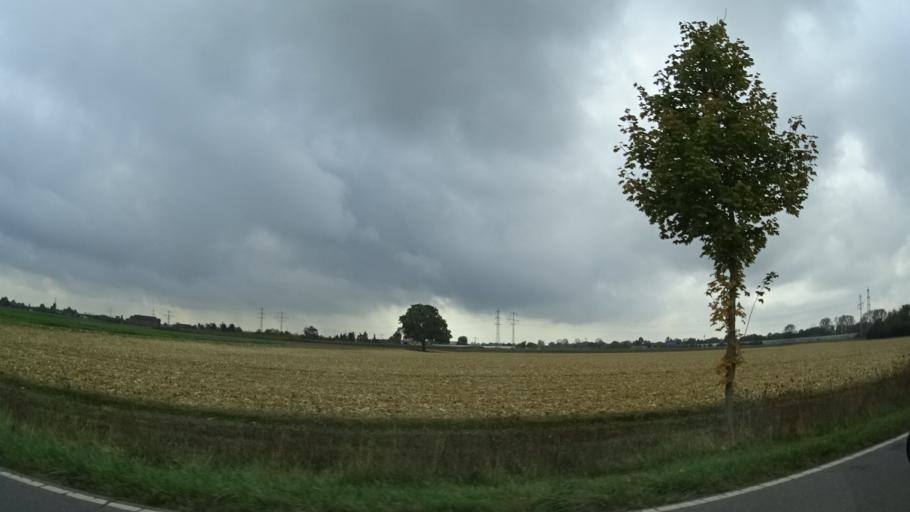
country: DE
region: Baden-Wuerttemberg
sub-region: Karlsruhe Region
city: Eppelheim
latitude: 49.3834
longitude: 8.6435
